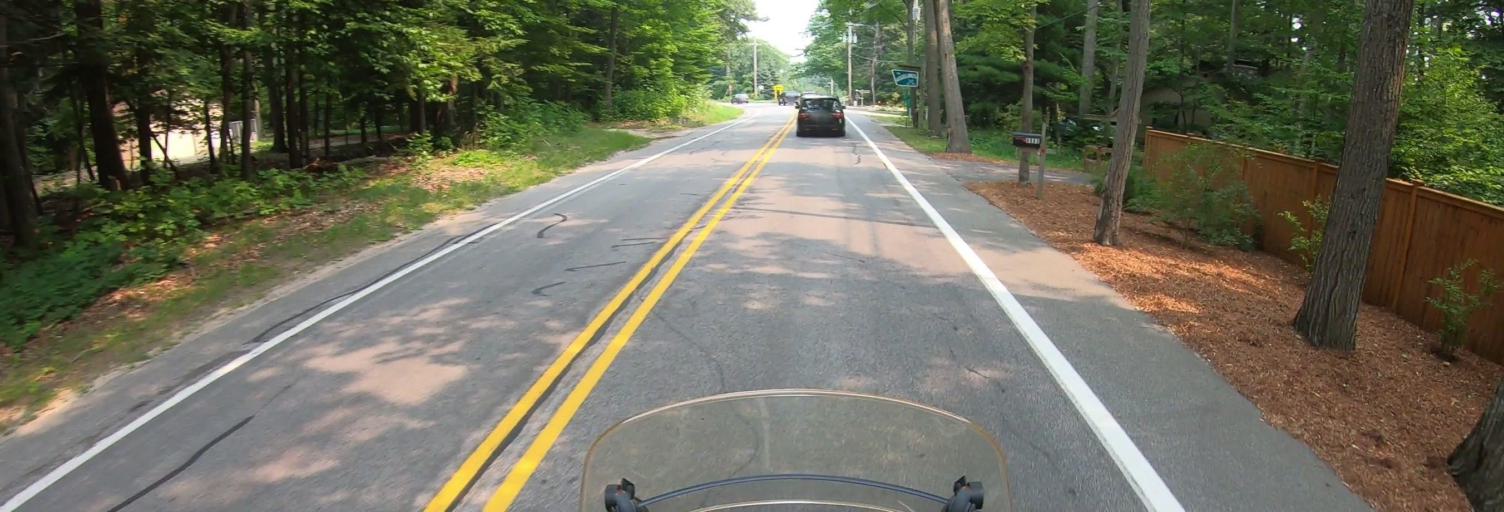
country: US
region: Michigan
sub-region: Leelanau County
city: Leland
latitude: 44.8824
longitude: -85.9890
